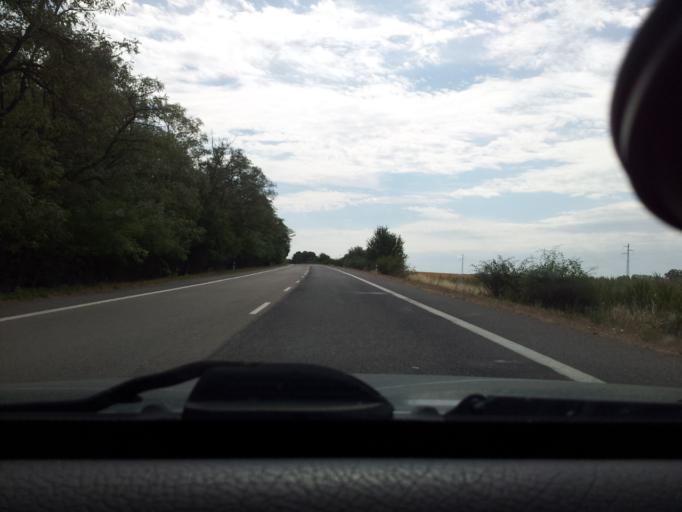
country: SK
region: Nitriansky
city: Zlate Moravce
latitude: 48.3651
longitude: 18.4480
